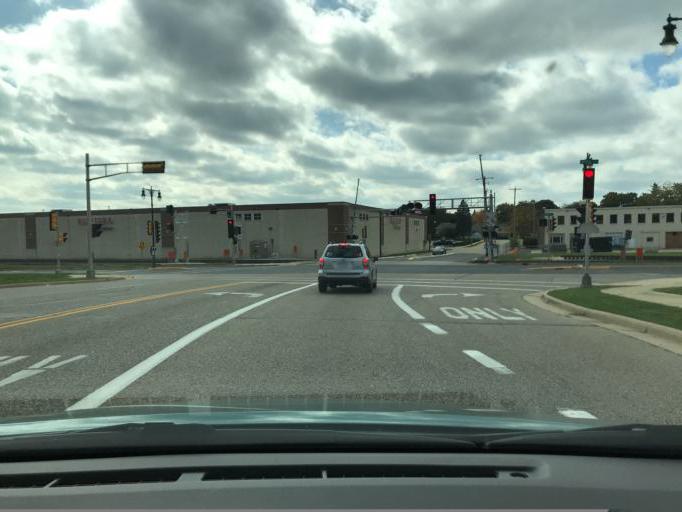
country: US
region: Wisconsin
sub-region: Racine County
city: Burlington
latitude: 42.6772
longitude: -88.2710
